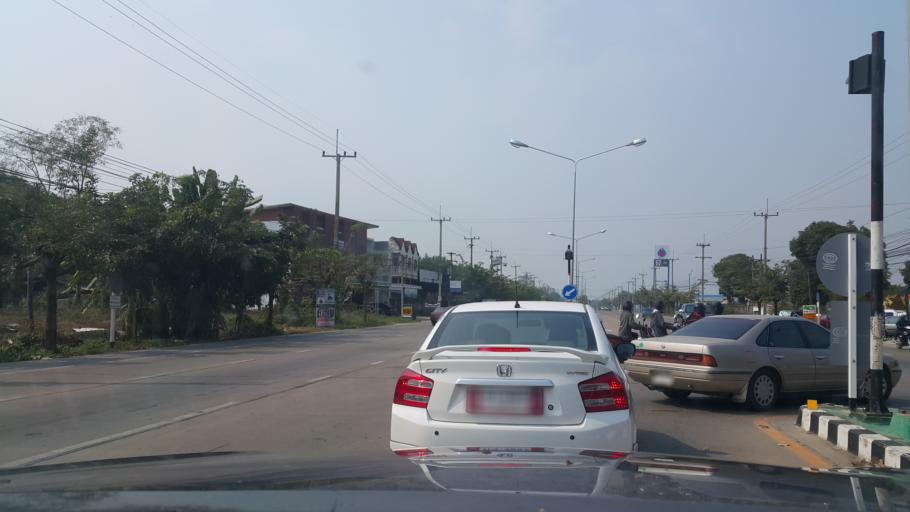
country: TH
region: Phitsanulok
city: Phitsanulok
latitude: 16.8421
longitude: 100.2328
